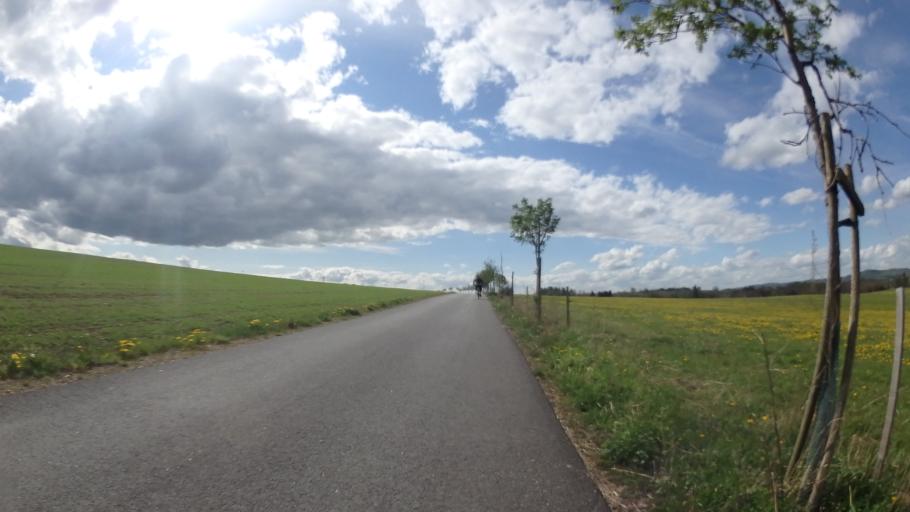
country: CZ
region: Vysocina
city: Merin
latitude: 49.3569
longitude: 15.9241
